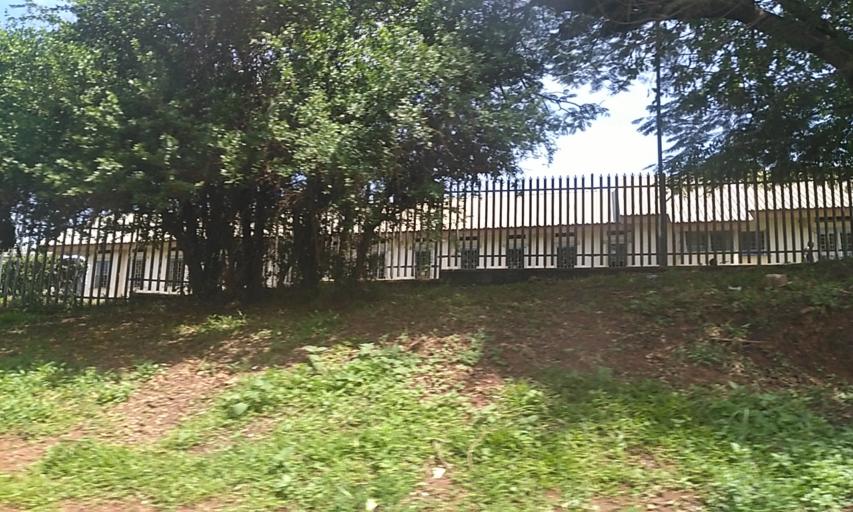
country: UG
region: Central Region
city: Kampala Central Division
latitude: 0.3427
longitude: 32.5767
